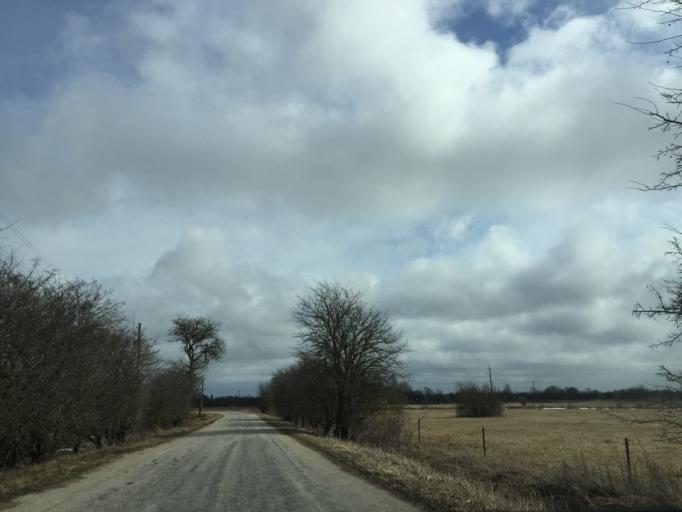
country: EE
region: Laeaene
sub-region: Lihula vald
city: Lihula
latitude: 58.7347
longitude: 23.8474
